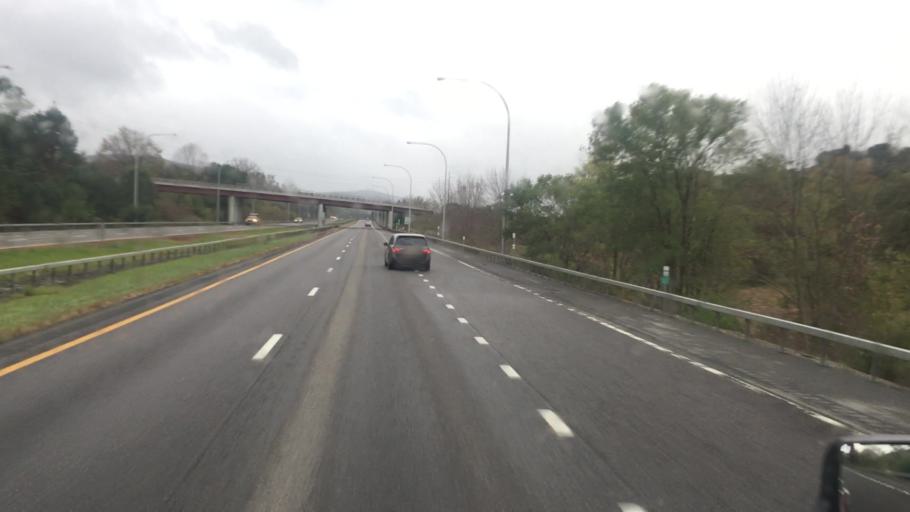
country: US
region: New York
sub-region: Broome County
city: Endwell
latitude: 42.1122
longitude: -76.0053
